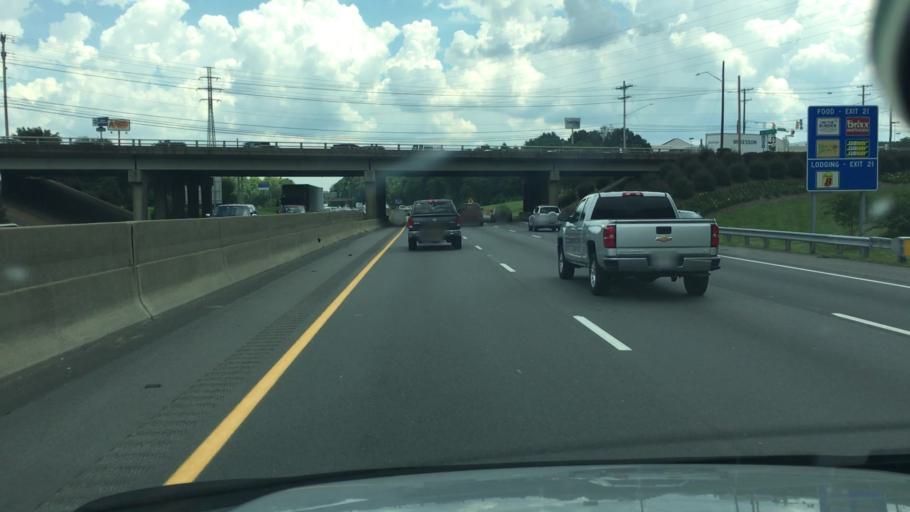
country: US
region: North Carolina
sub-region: Gaston County
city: Ranlo
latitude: 35.2692
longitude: -81.1503
